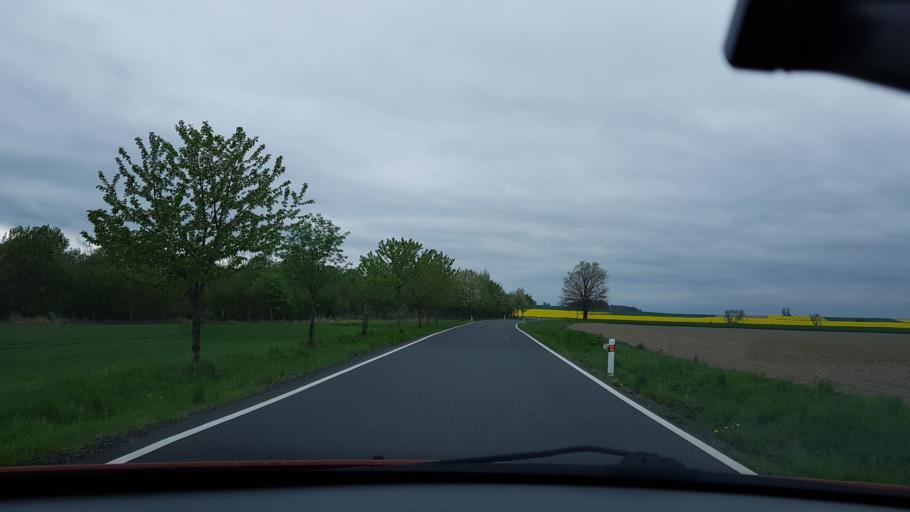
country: CZ
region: Olomoucky
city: Vidnava
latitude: 50.3804
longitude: 17.1554
